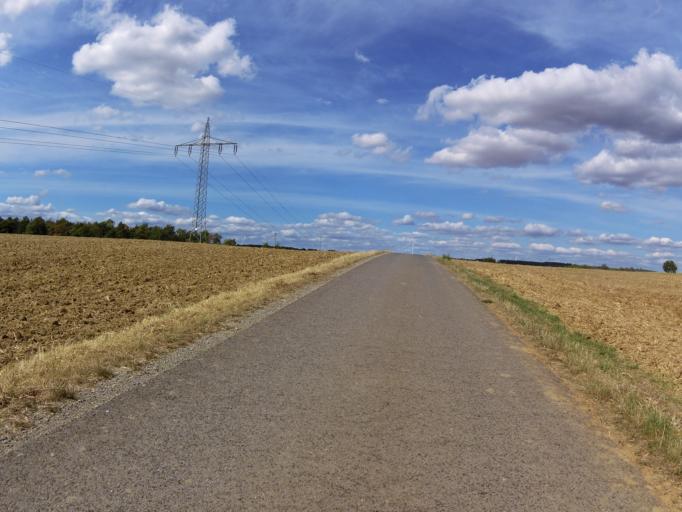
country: DE
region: Bavaria
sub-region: Regierungsbezirk Unterfranken
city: Guntersleben
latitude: 49.8673
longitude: 9.9147
